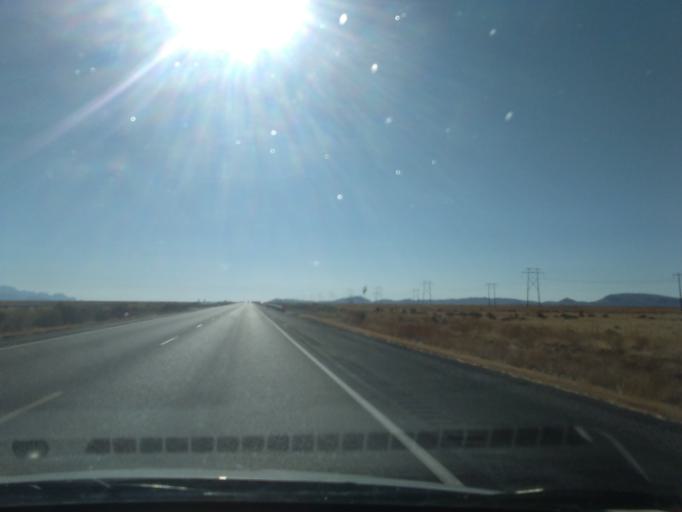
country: US
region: New Mexico
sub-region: Luna County
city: Deming
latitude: 32.4792
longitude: -107.5291
